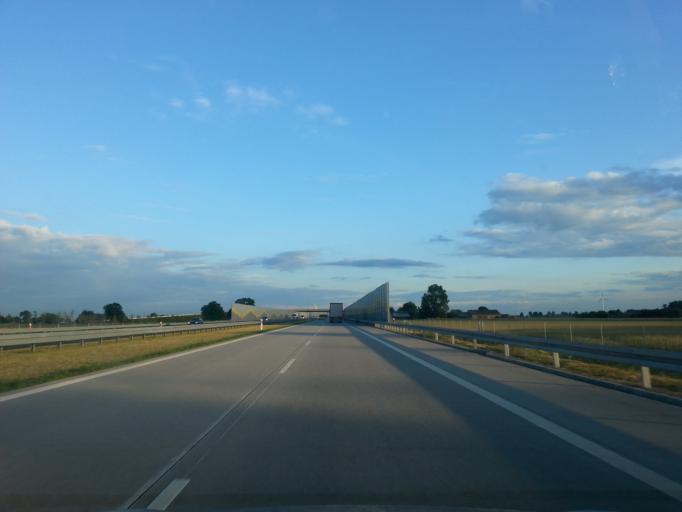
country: PL
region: Lodz Voivodeship
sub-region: Powiat sieradzki
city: Zloczew
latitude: 51.4321
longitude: 18.6457
